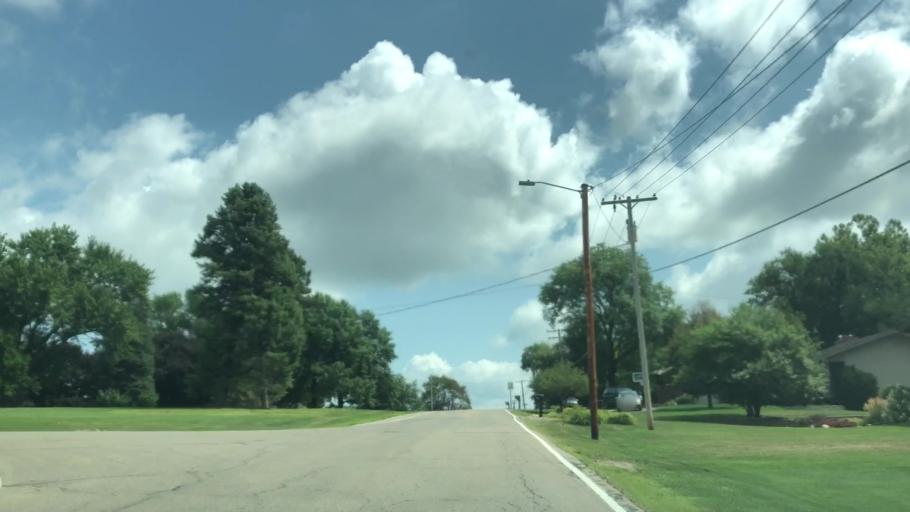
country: US
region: Iowa
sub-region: Marshall County
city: Marshalltown
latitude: 42.0286
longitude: -92.9343
